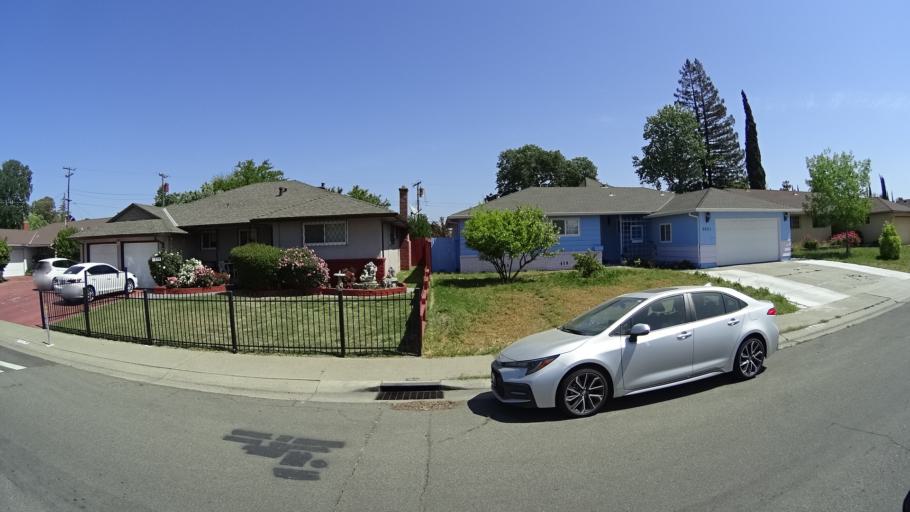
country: US
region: California
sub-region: Sacramento County
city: Parkway
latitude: 38.4986
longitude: -121.4867
